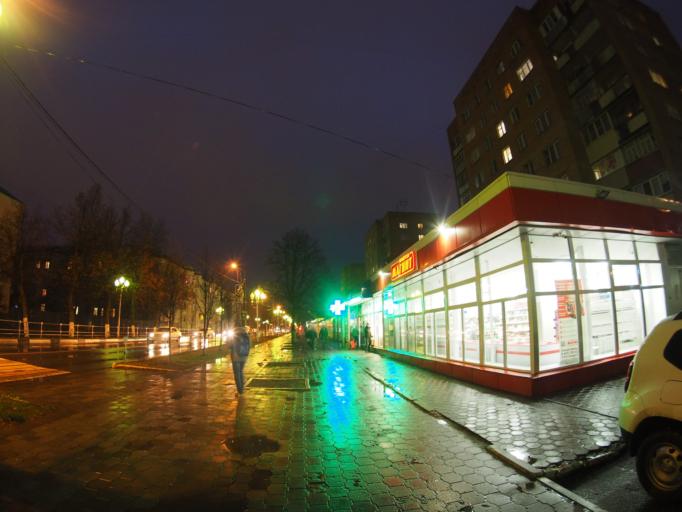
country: RU
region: Moskovskaya
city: Stupino
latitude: 54.8866
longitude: 38.0815
